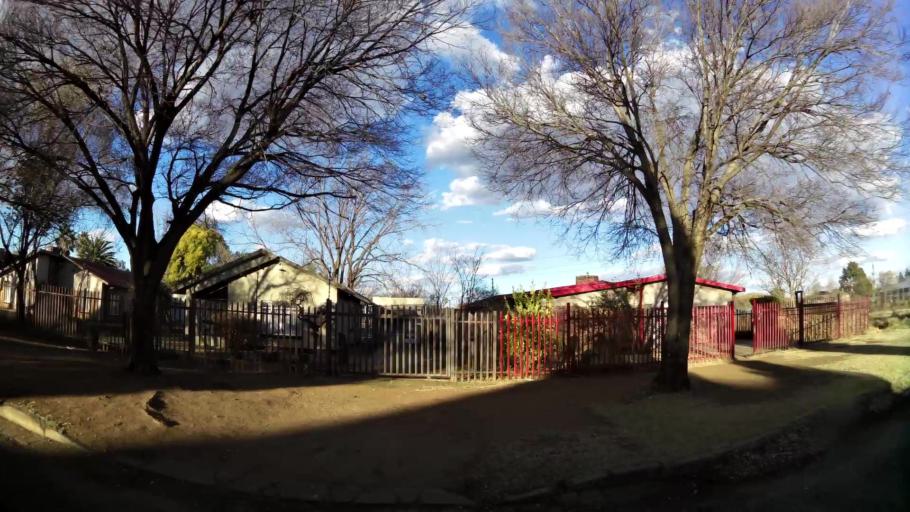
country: ZA
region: North-West
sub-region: Dr Kenneth Kaunda District Municipality
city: Potchefstroom
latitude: -26.7035
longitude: 27.0868
